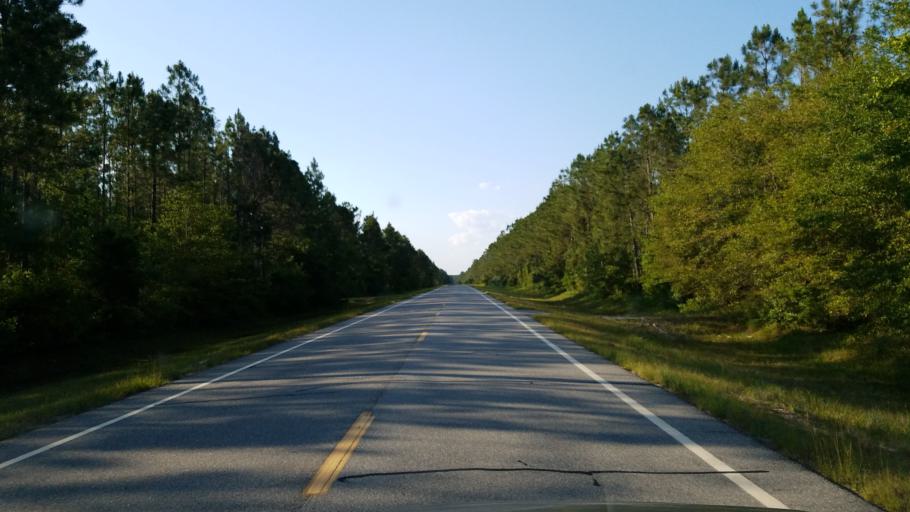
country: US
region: Georgia
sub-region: Echols County
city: Statenville
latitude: 30.8703
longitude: -83.0522
